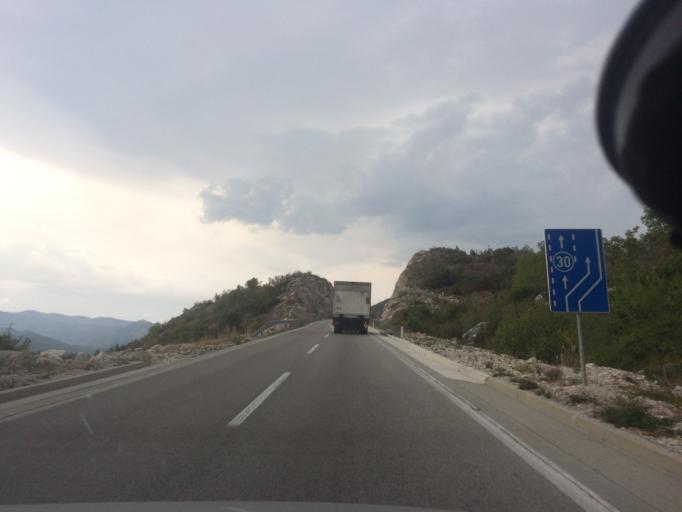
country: ME
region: Kotor
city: Risan
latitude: 42.6558
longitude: 18.6721
